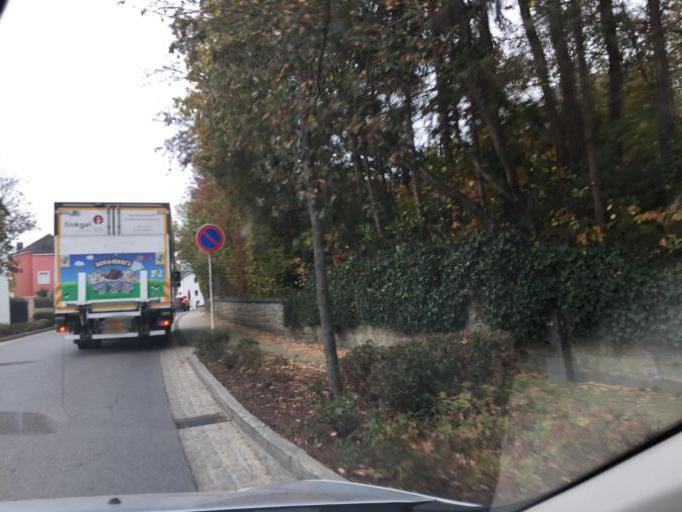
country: LU
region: Luxembourg
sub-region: Canton de Luxembourg
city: Olm
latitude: 49.6565
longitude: 5.9992
